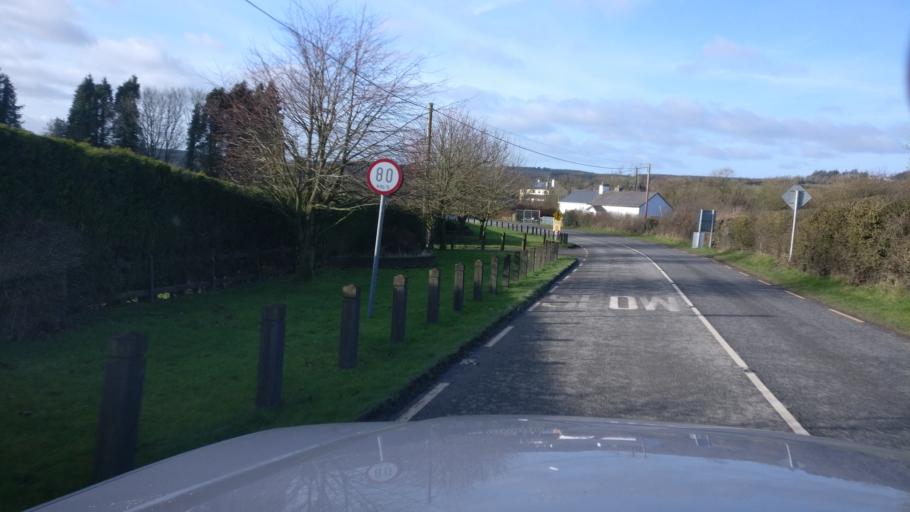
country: IE
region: Leinster
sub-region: Kilkenny
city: Castlecomer
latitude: 52.8894
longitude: -7.1611
